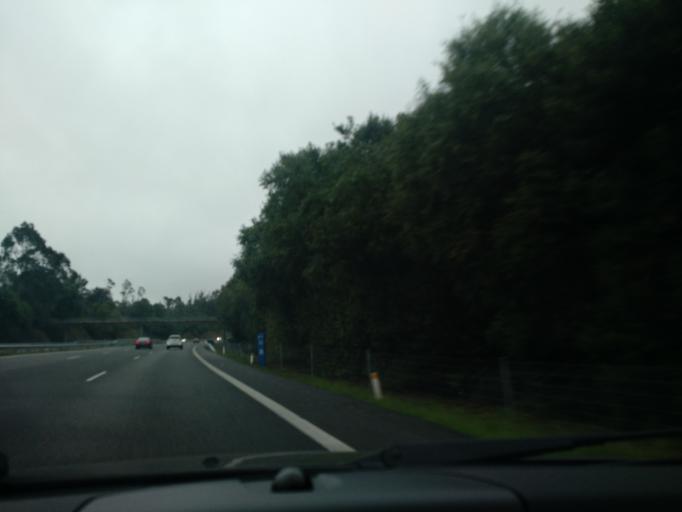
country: ES
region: Galicia
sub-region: Provincia da Coruna
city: Abegondo
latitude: 43.1739
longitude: -8.3136
